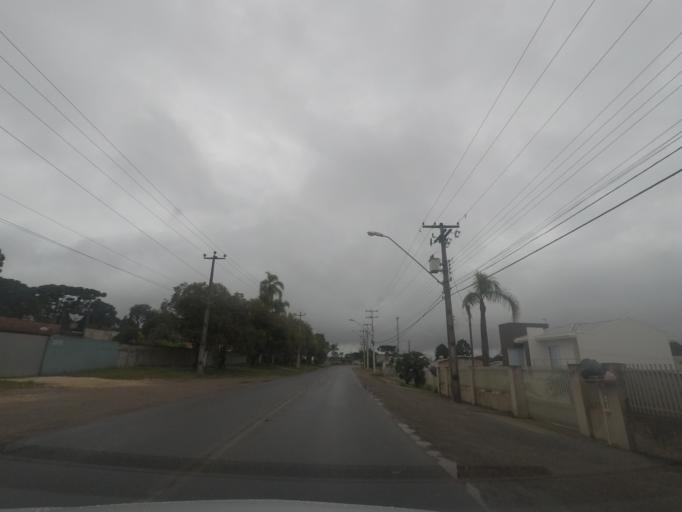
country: BR
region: Parana
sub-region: Quatro Barras
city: Quatro Barras
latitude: -25.3391
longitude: -49.0804
